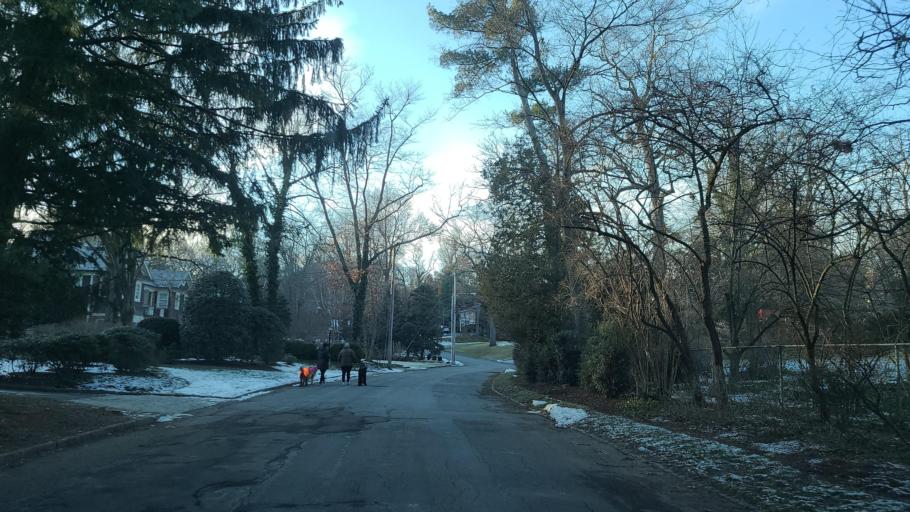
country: US
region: New Jersey
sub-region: Essex County
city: Short Hills
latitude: 40.7302
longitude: -74.3319
